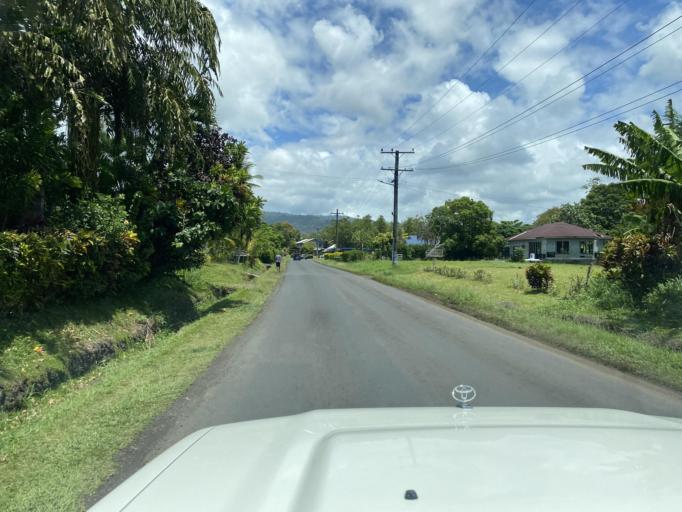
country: WS
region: Tuamasaga
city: Apia
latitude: -13.8441
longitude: -171.7764
